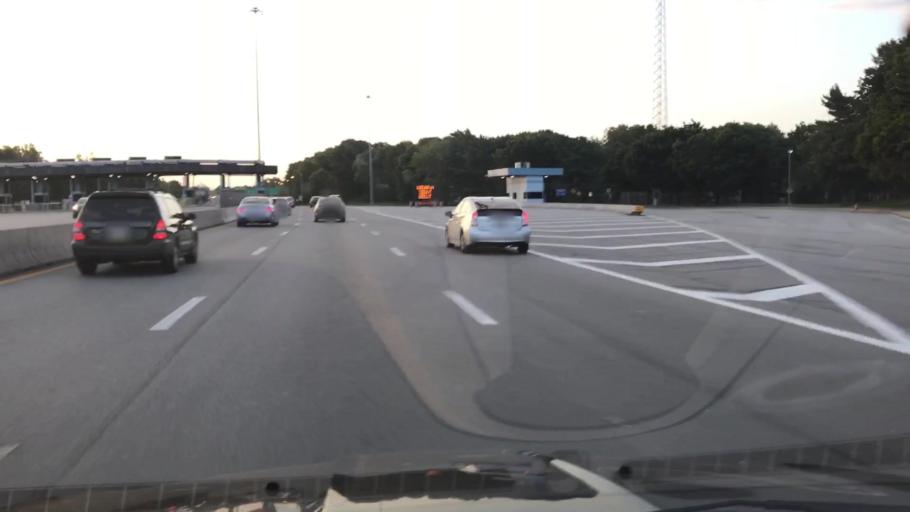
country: US
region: New Jersey
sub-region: Camden County
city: Pennsauken
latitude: 39.9798
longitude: -75.0545
